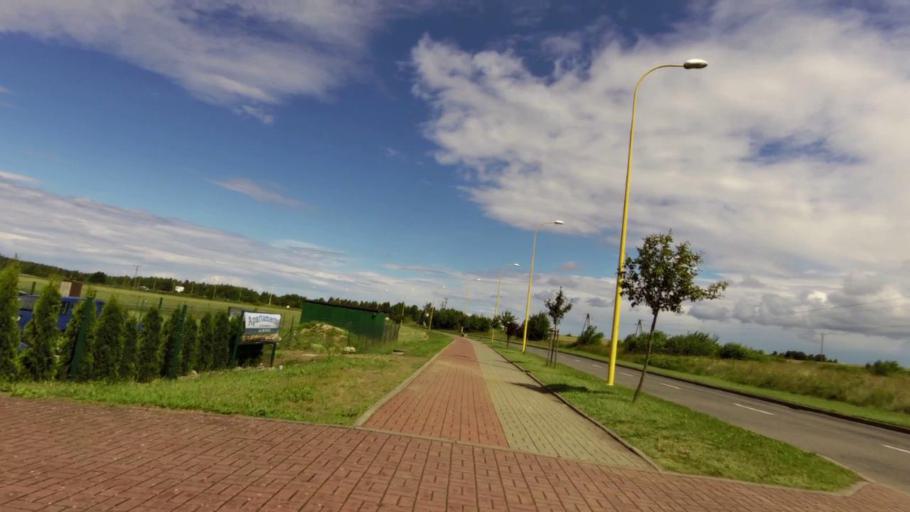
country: PL
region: West Pomeranian Voivodeship
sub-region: Powiat slawienski
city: Darlowo
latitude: 54.4410
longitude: 16.4068
